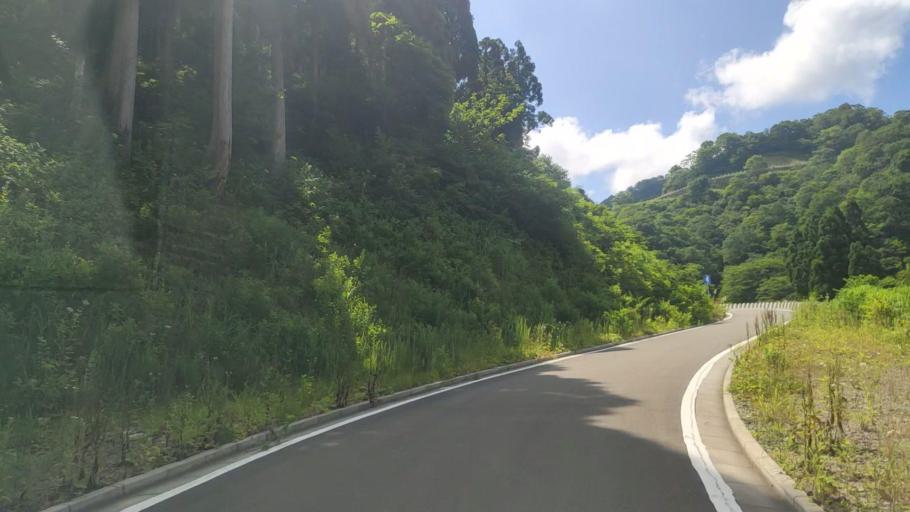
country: JP
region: Fukui
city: Katsuyama
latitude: 36.1559
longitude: 136.5271
